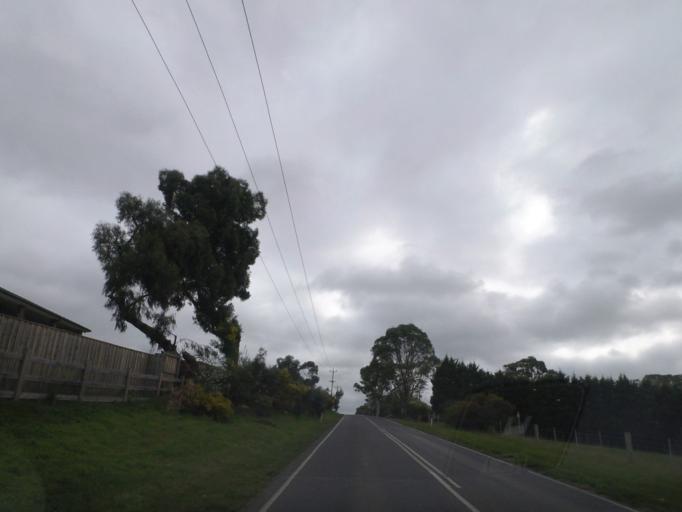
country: AU
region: Victoria
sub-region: Nillumbik
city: Doreen
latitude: -37.5995
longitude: 145.1392
